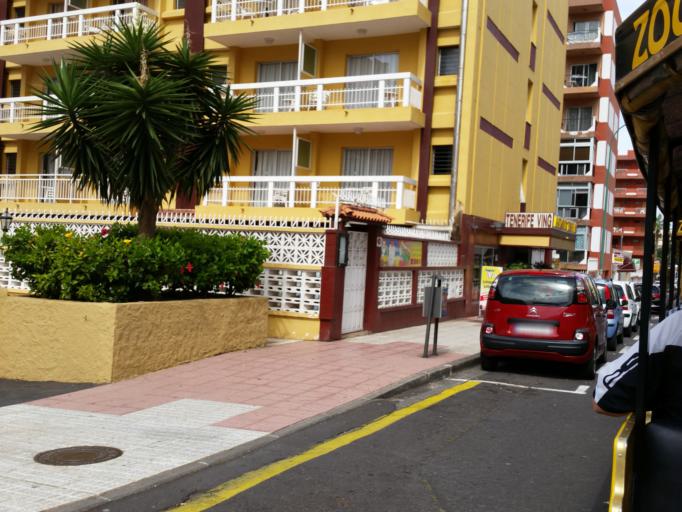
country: ES
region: Canary Islands
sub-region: Provincia de Santa Cruz de Tenerife
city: Puerto de la Cruz
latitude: 28.4121
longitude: -16.5561
